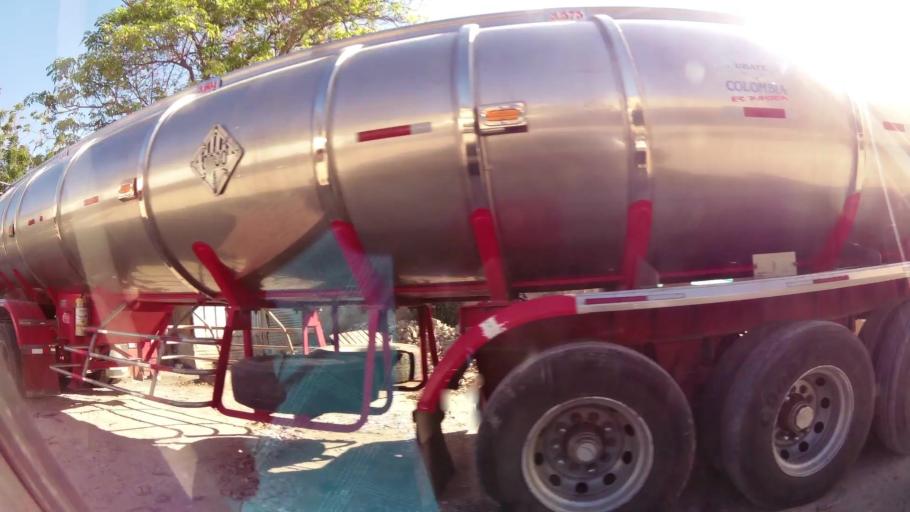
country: CO
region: Atlantico
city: Barranquilla
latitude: 10.9933
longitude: -74.7812
